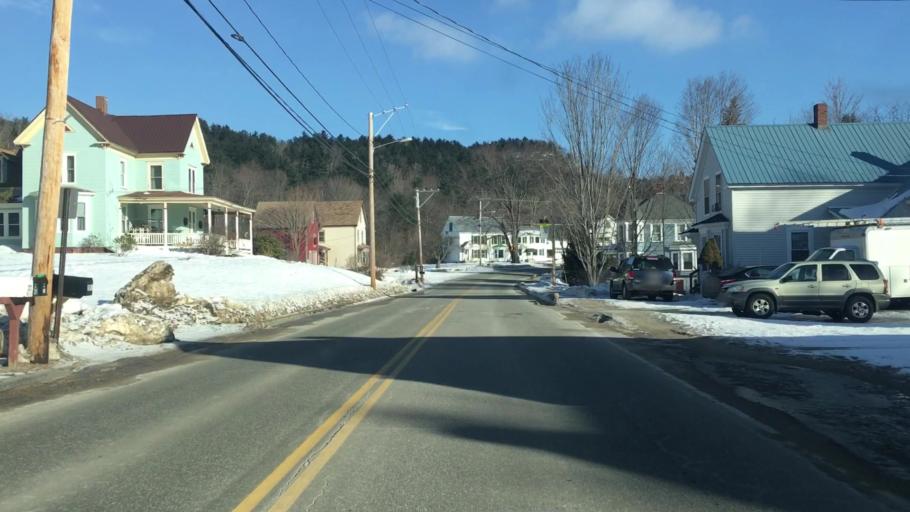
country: US
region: Maine
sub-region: Oxford County
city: West Paris
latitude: 44.3261
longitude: -70.5724
